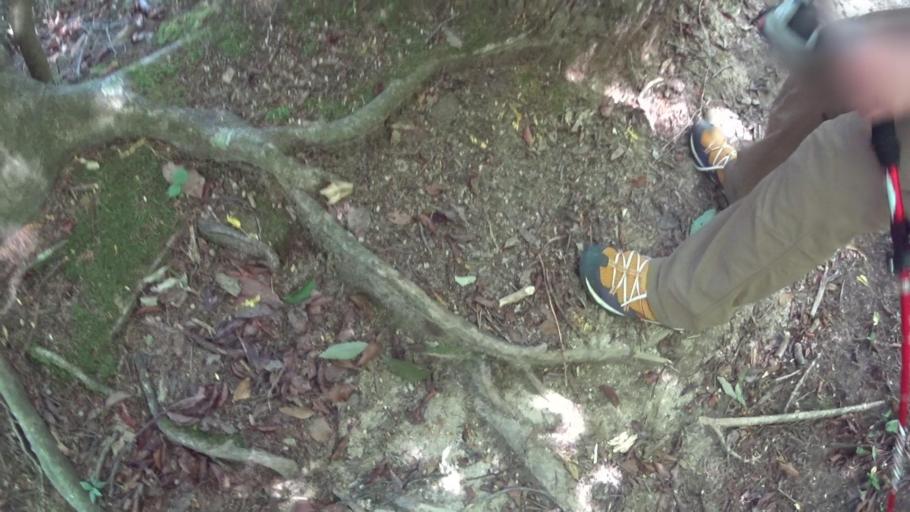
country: JP
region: Kyoto
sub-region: Kyoto-shi
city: Kamigyo-ku
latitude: 35.0398
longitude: 135.8032
